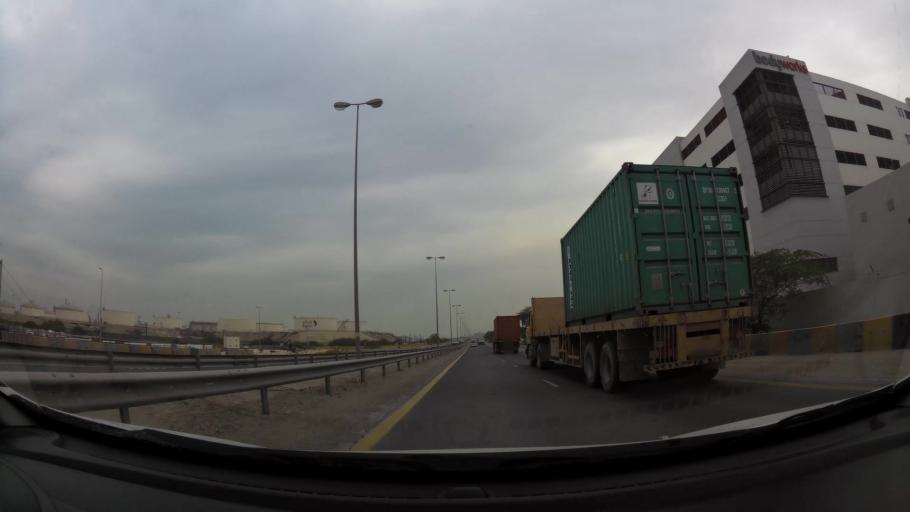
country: BH
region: Northern
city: Ar Rifa'
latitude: 26.1178
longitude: 50.5935
